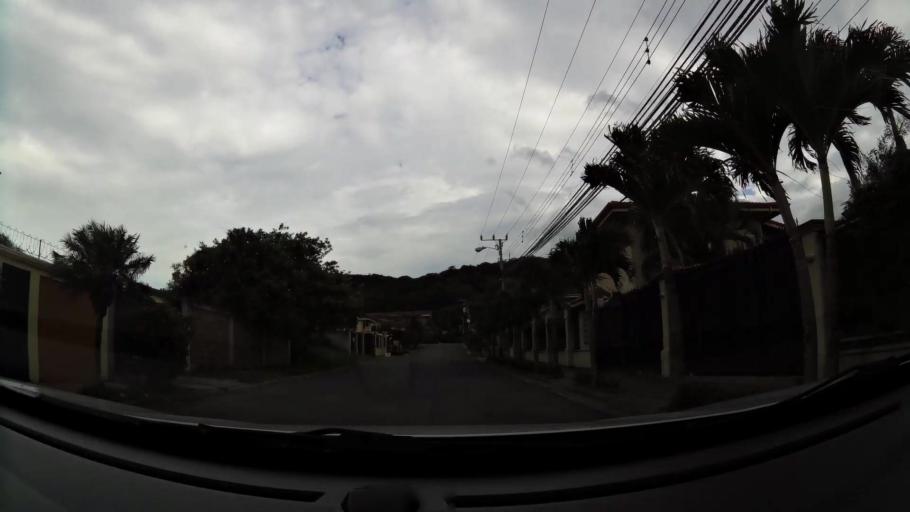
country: CR
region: San Jose
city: Santa Ana
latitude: 9.9525
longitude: -84.1881
